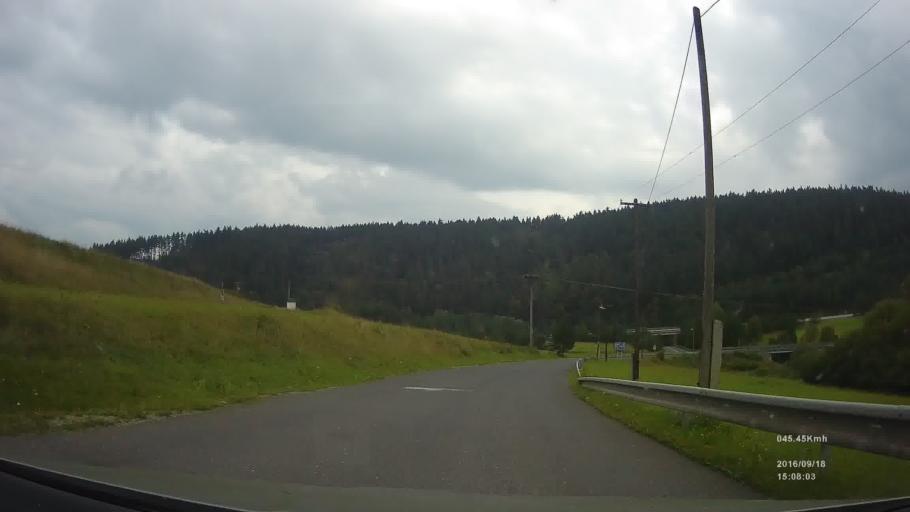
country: SK
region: Presovsky
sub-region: Okres Presov
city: Levoca
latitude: 49.0208
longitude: 20.5250
